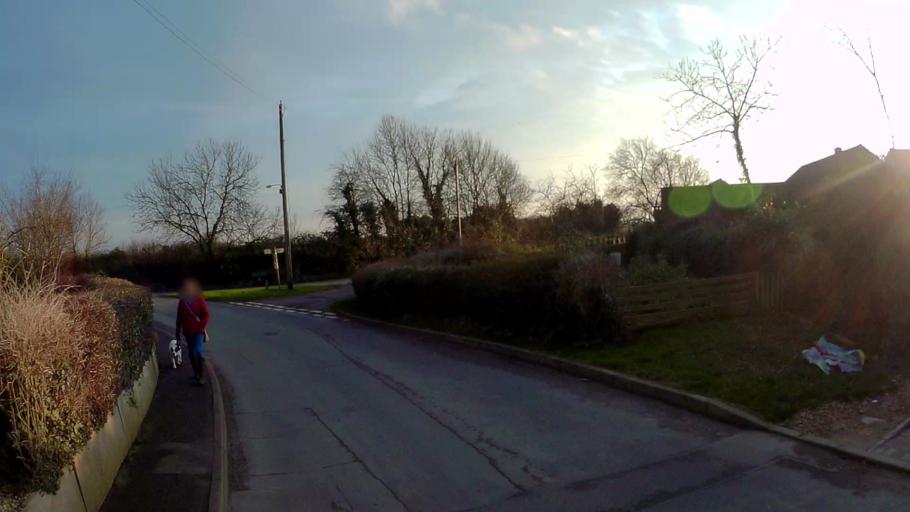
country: GB
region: England
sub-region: Lincolnshire
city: Bourne
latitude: 52.8021
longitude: -0.3889
